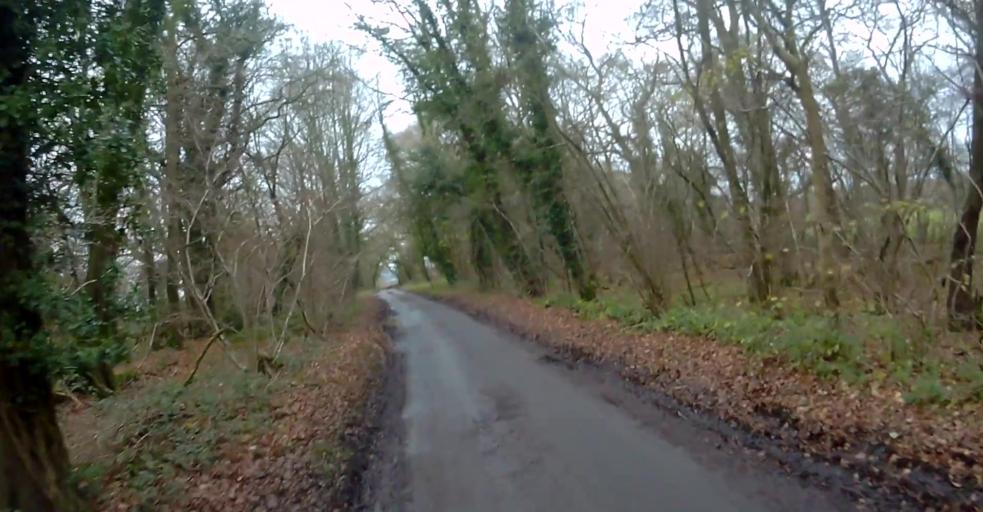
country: GB
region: England
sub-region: Hampshire
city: Overton
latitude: 51.2309
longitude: -1.2445
